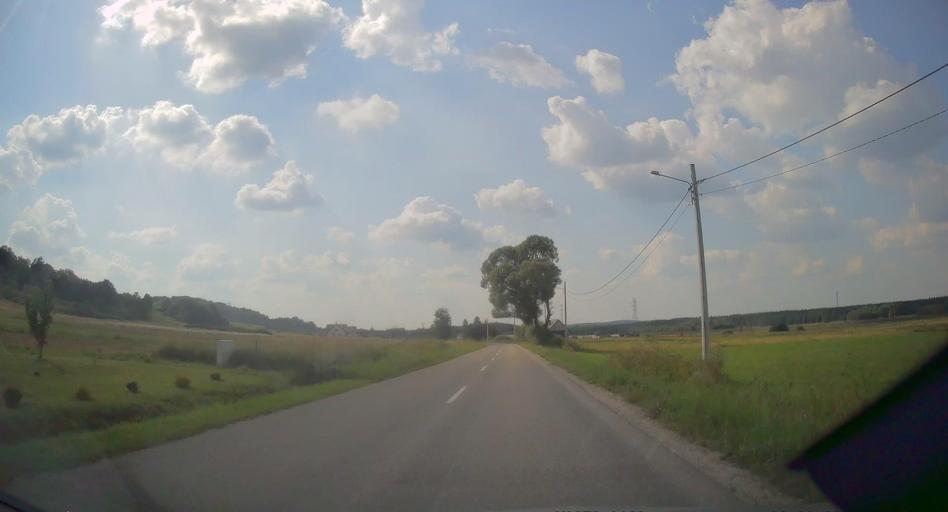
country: PL
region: Swietokrzyskie
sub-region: Powiat jedrzejowski
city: Malogoszcz
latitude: 50.8611
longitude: 20.3433
